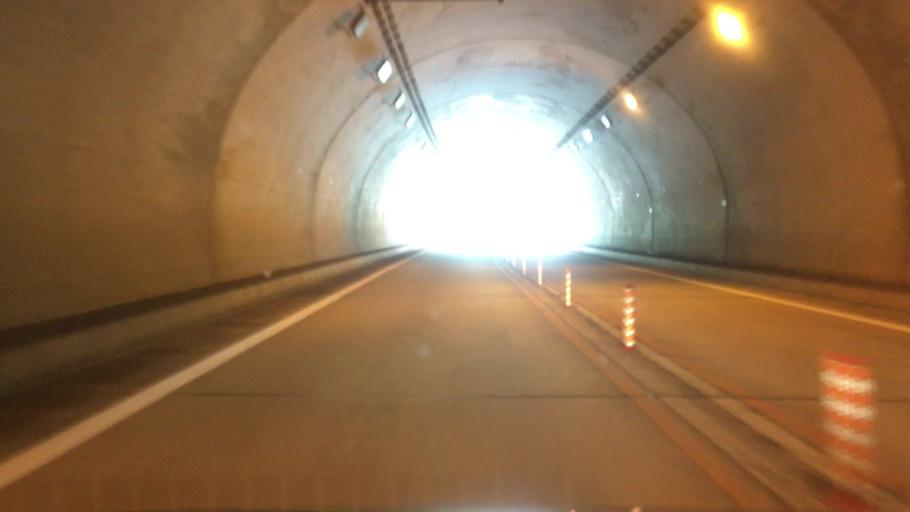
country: JP
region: Hyogo
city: Toyooka
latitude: 35.6284
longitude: 134.6093
